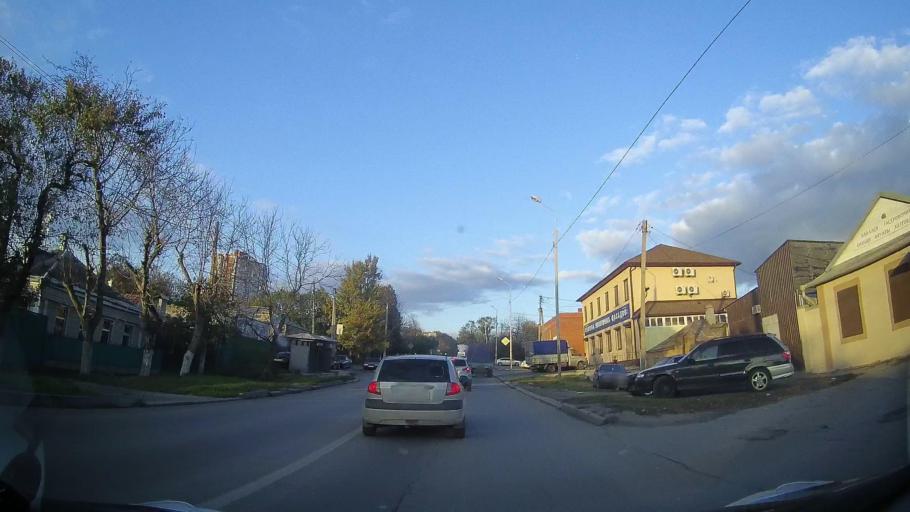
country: RU
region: Rostov
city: Imeni Chkalova
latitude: 47.2721
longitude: 39.7807
